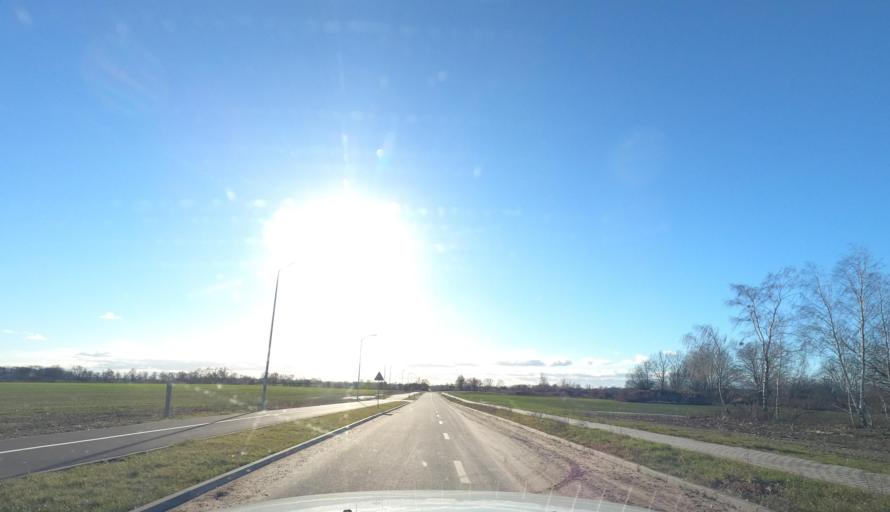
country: PL
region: West Pomeranian Voivodeship
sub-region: Powiat pyrzycki
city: Warnice
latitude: 53.2779
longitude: 14.9894
